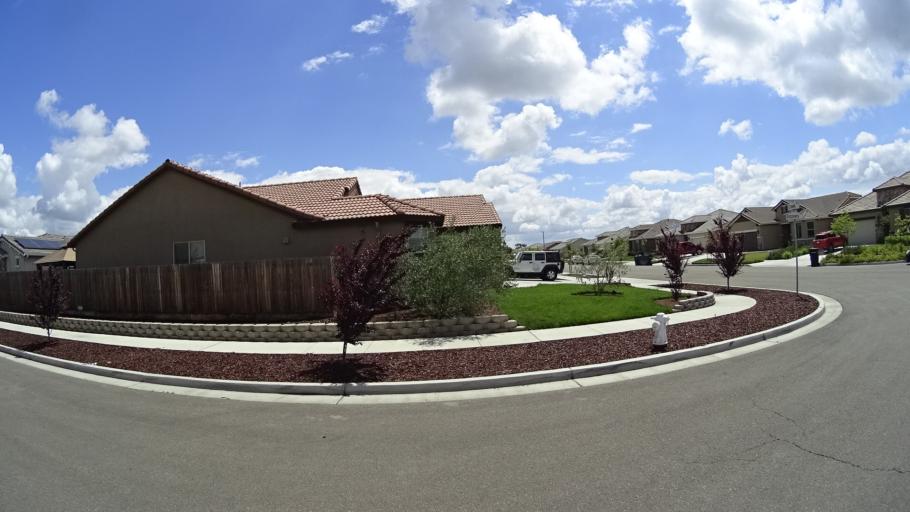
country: US
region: California
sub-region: Kings County
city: Lucerne
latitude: 36.3700
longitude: -119.6632
